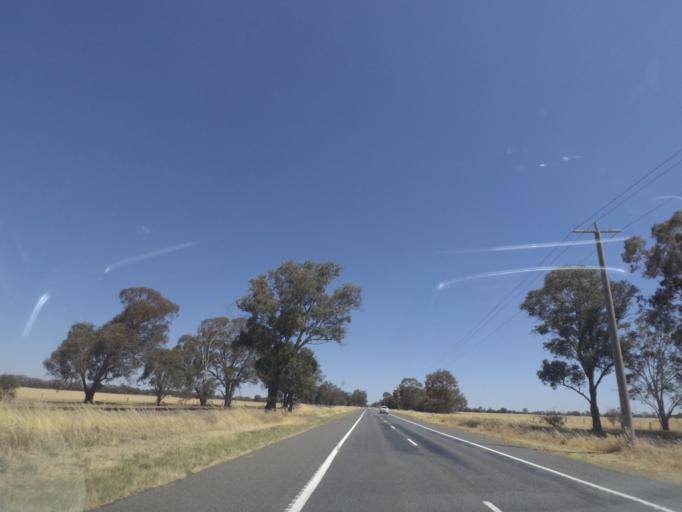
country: AU
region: Victoria
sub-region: Greater Shepparton
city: Shepparton
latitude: -36.2037
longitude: 145.4318
